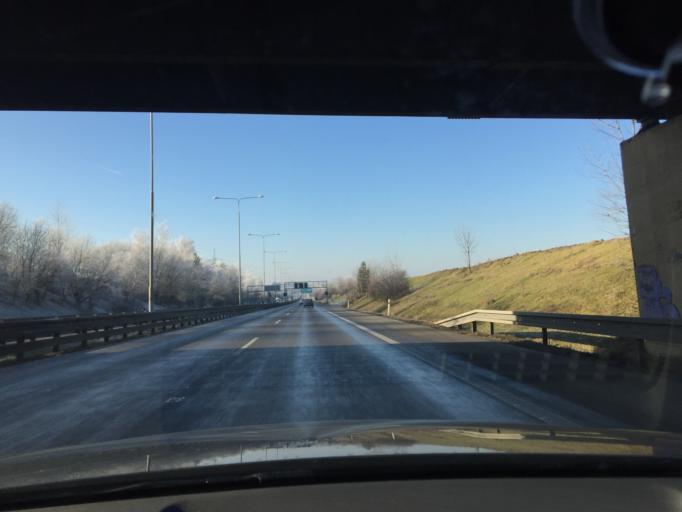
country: CZ
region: Central Bohemia
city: Trebotov
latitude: 50.0241
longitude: 14.3164
